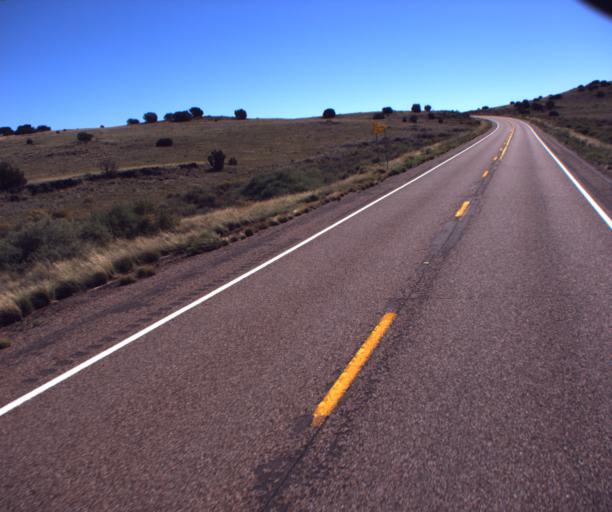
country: US
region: Arizona
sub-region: Apache County
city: Saint Johns
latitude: 34.5638
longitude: -109.5063
